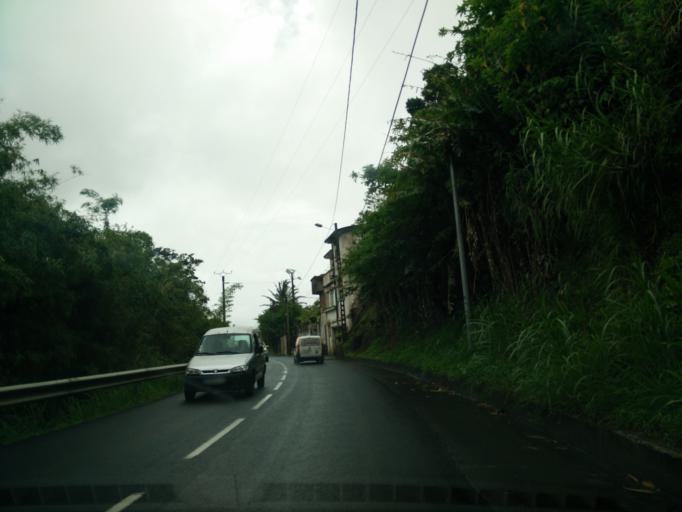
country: MQ
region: Martinique
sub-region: Martinique
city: Saint-Joseph
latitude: 14.6649
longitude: -61.0877
